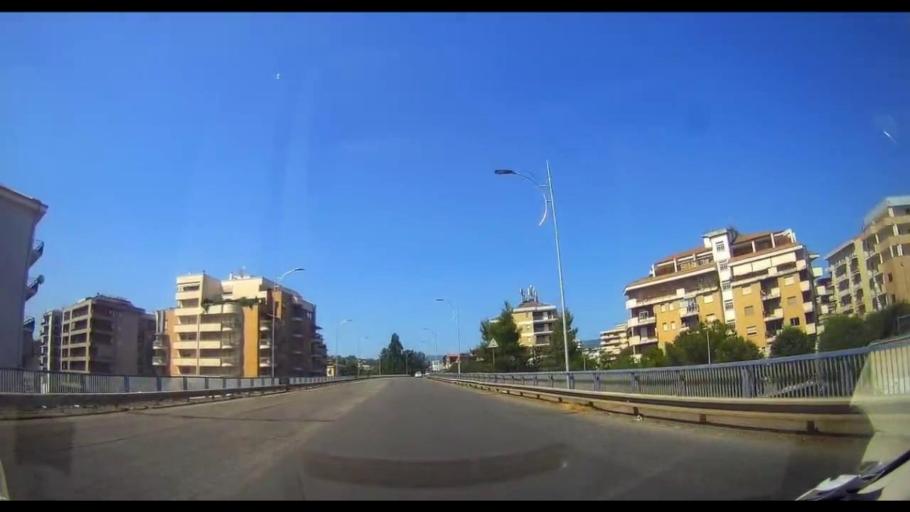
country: IT
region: Calabria
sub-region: Provincia di Cosenza
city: Cosenza
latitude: 39.3122
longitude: 16.2550
